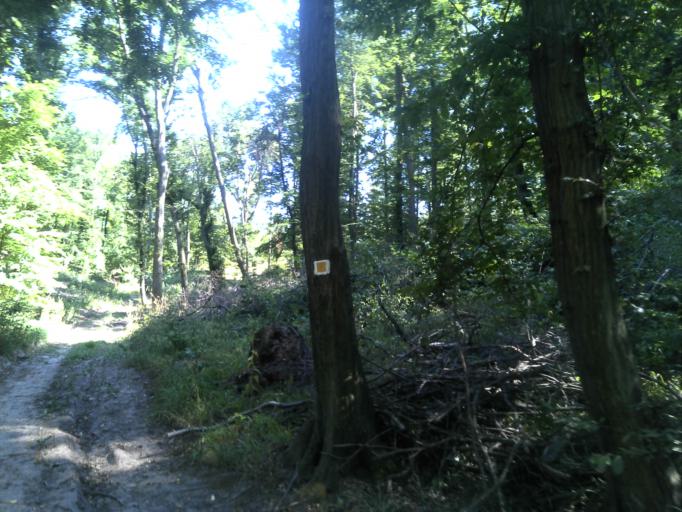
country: HU
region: Pest
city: Piliscsaba
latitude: 47.6330
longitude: 18.8612
